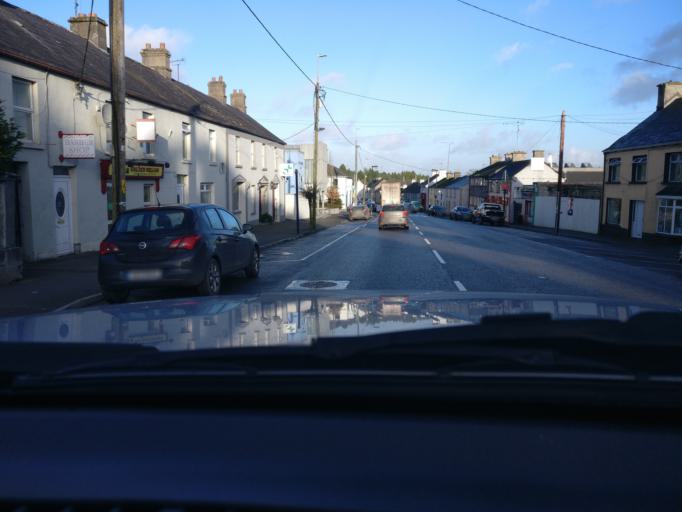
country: IE
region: Leinster
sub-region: An Iarmhi
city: Rathwire
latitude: 53.6118
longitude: -7.0932
